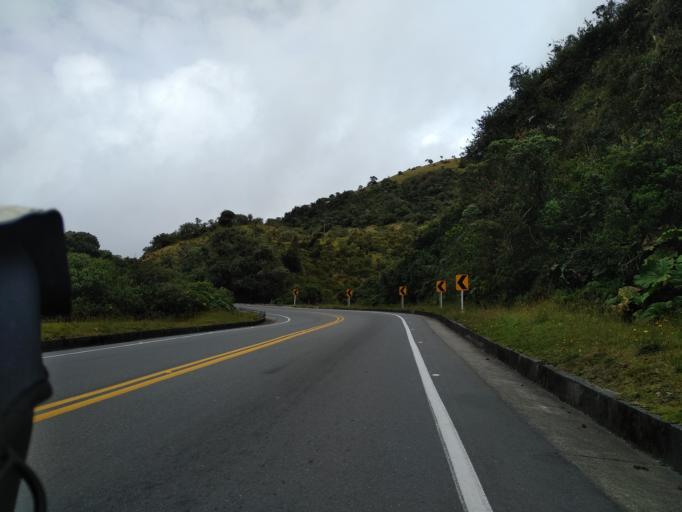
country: CO
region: Tolima
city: Herveo
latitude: 5.0742
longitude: -75.2840
